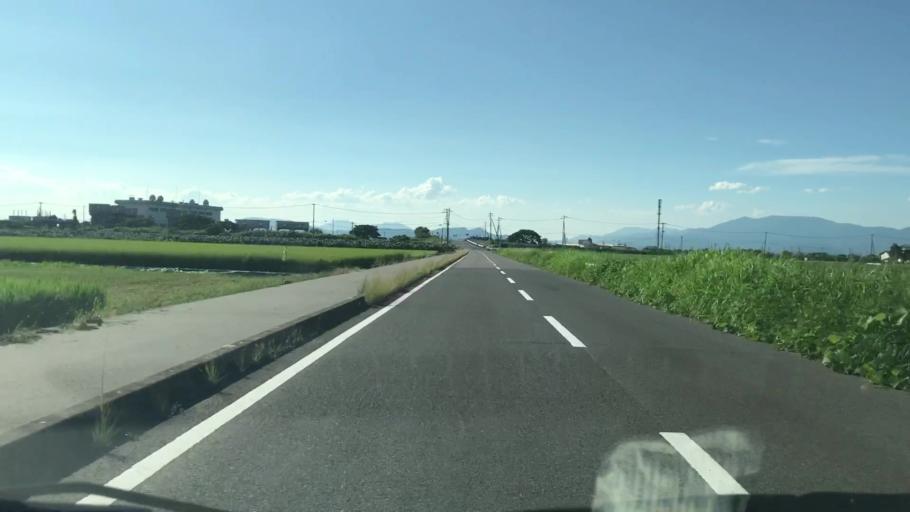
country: JP
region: Saga Prefecture
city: Okawa
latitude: 33.1845
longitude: 130.2947
